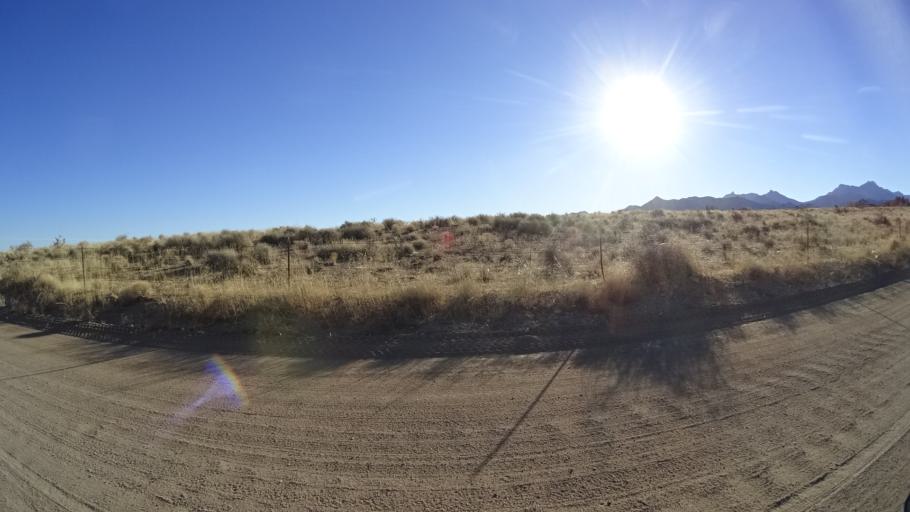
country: US
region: Arizona
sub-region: Mohave County
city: Kingman
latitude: 35.1980
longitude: -113.9939
